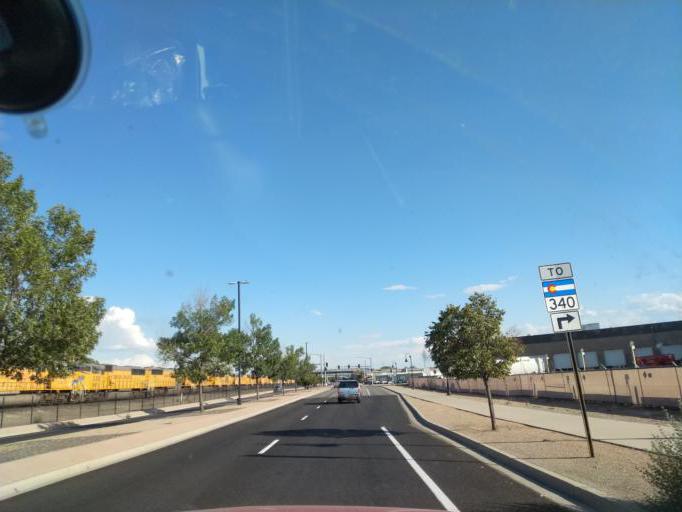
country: US
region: Colorado
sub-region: Mesa County
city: Grand Junction
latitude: 39.0717
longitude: -108.5804
